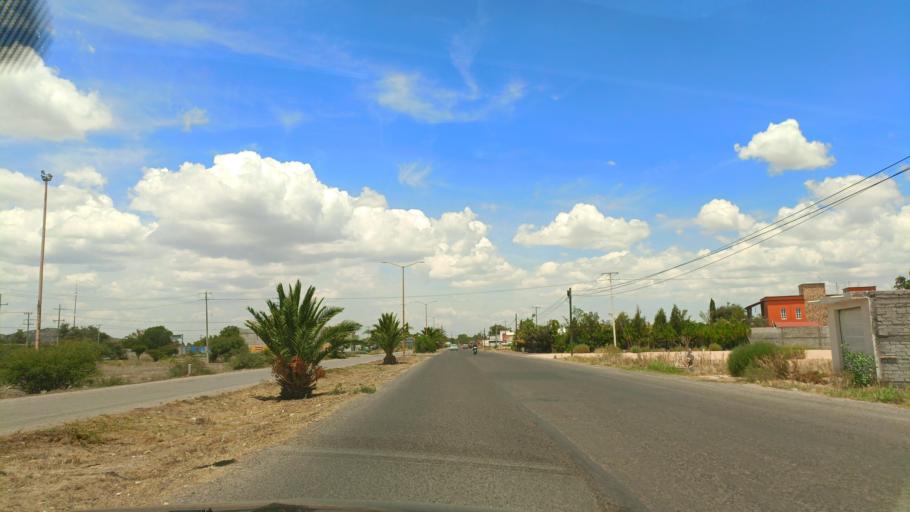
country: MX
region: Guanajuato
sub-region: San Luis de la Paz
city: San Ignacio
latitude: 21.2888
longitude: -100.5530
